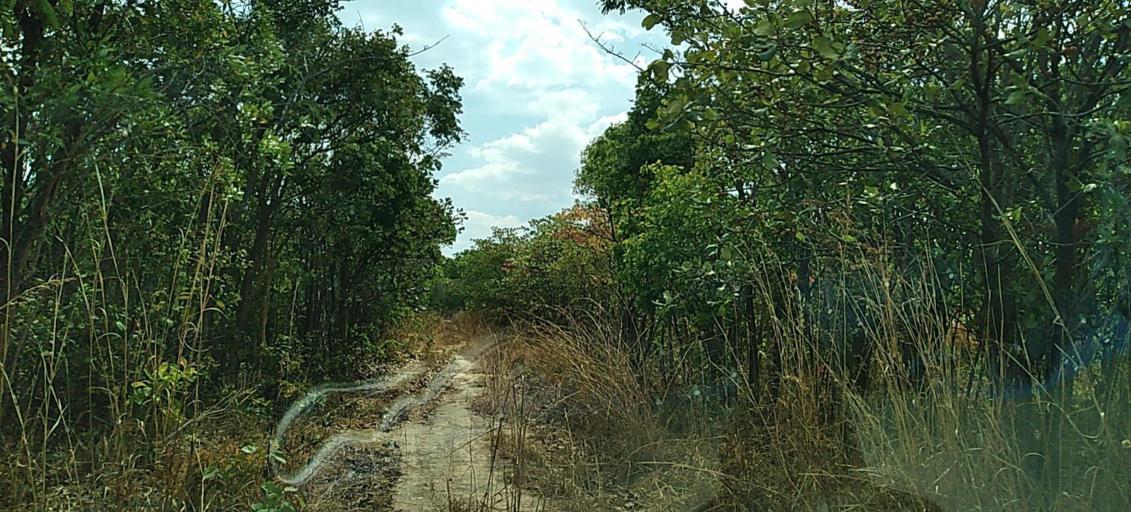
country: ZM
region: Copperbelt
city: Chililabombwe
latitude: -12.3322
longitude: 27.7628
